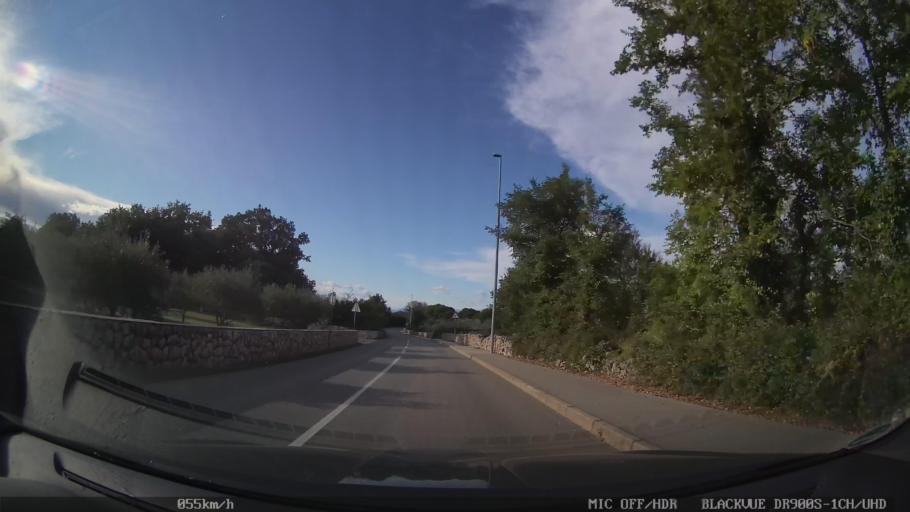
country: HR
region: Primorsko-Goranska
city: Njivice
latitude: 45.1082
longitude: 14.5246
